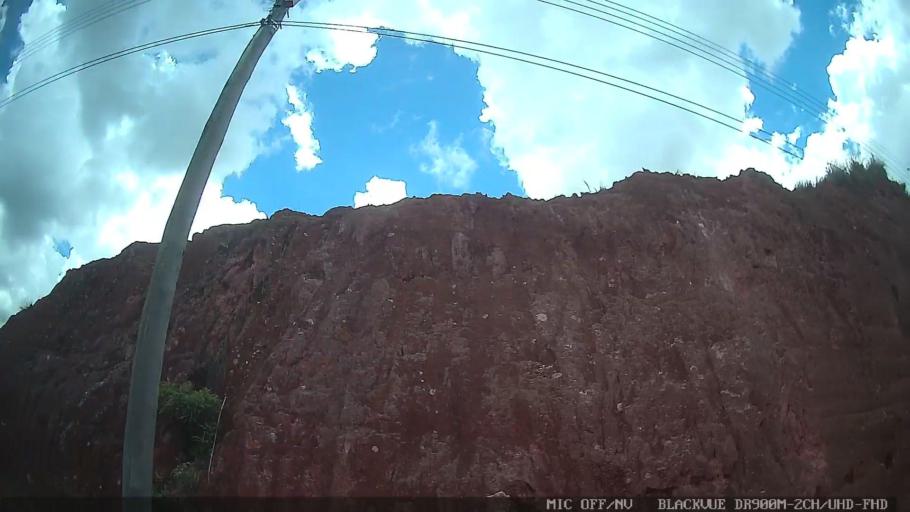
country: BR
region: Sao Paulo
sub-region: Serra Negra
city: Serra Negra
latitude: -22.5981
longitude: -46.6989
